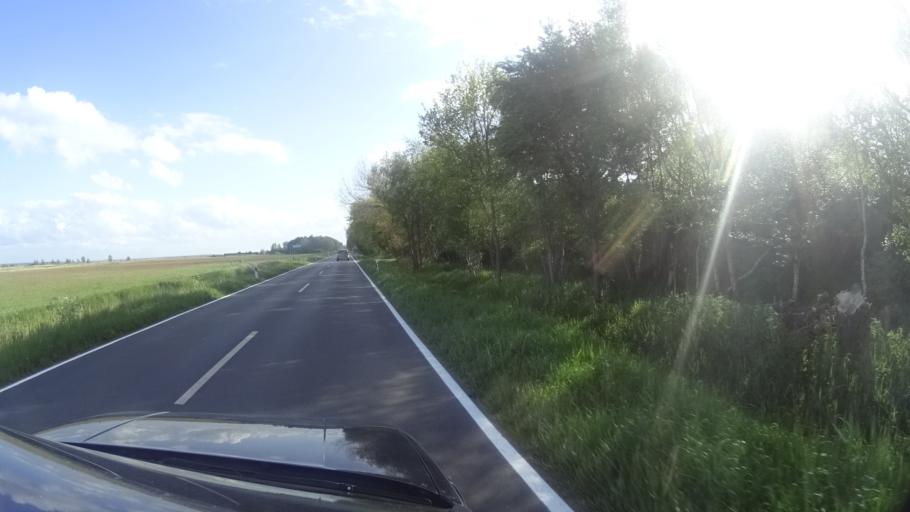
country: DE
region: Mecklenburg-Vorpommern
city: Ostseebad Dierhagen
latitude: 54.3384
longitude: 12.3790
